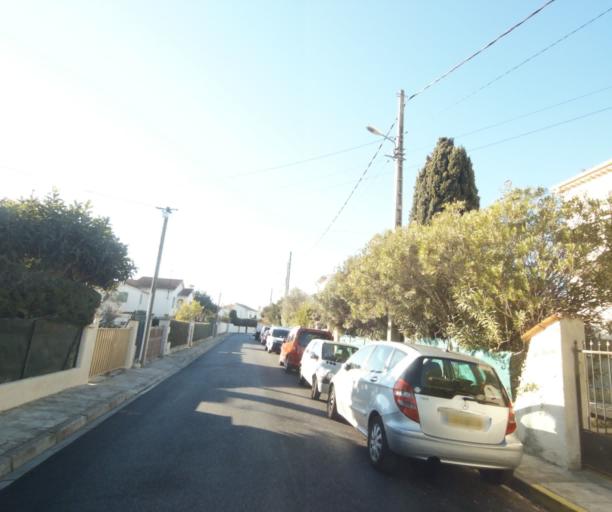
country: FR
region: Provence-Alpes-Cote d'Azur
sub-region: Departement des Alpes-Maritimes
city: Antibes
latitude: 43.5826
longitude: 7.1032
